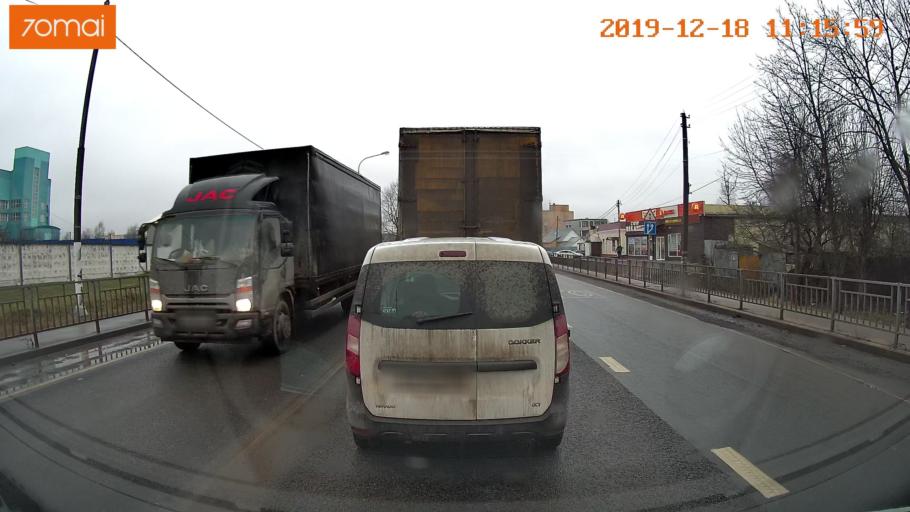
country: RU
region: Moskovskaya
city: Krasnoznamensk
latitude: 55.6281
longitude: 37.0210
